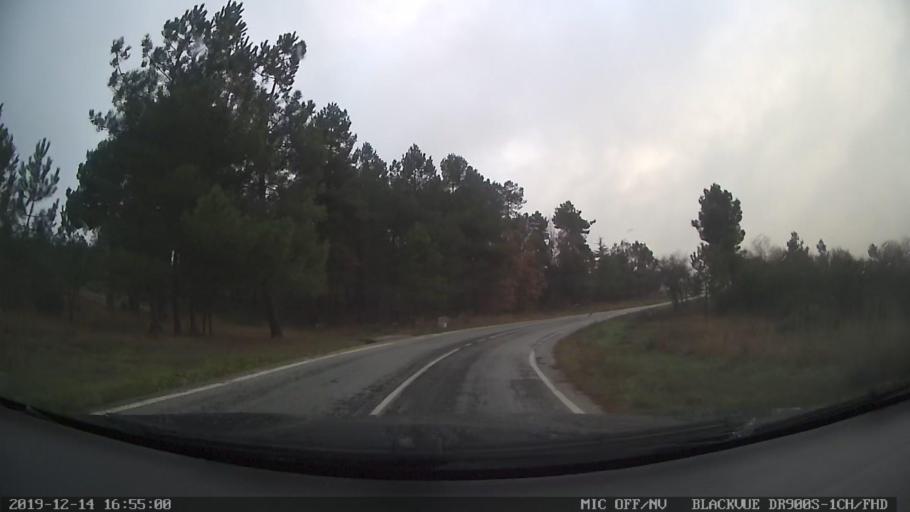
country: PT
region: Vila Real
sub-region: Murca
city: Murca
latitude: 41.4381
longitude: -7.5282
